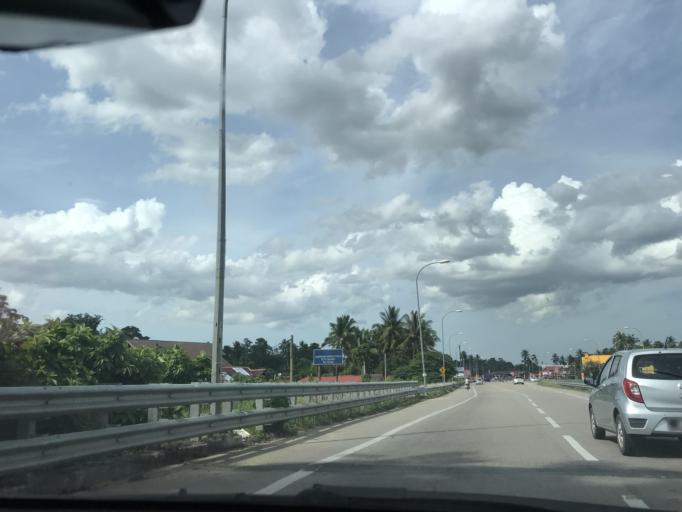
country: MY
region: Kelantan
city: Kampung Lemal
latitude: 6.0325
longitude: 102.1477
